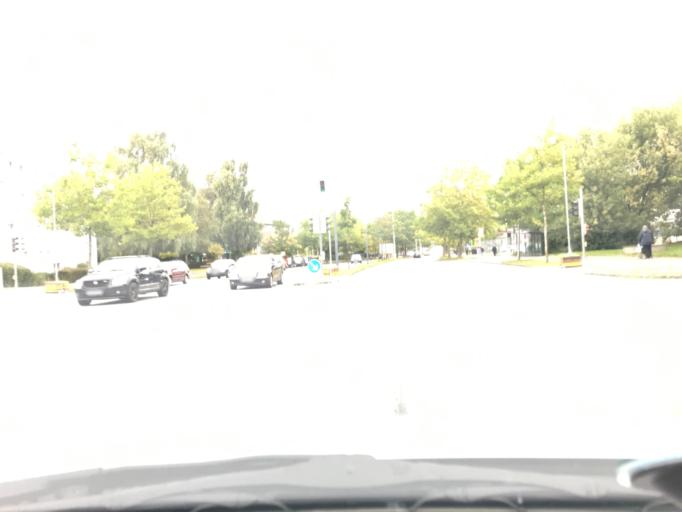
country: DE
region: Schleswig-Holstein
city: Melsdorf
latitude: 54.3194
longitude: 10.0502
